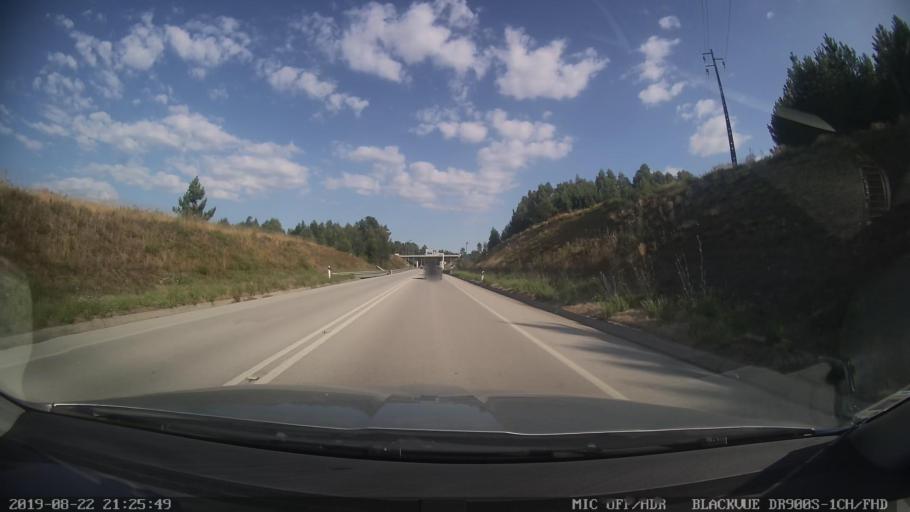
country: PT
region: Castelo Branco
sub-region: Serta
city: Serta
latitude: 39.8590
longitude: -8.1275
